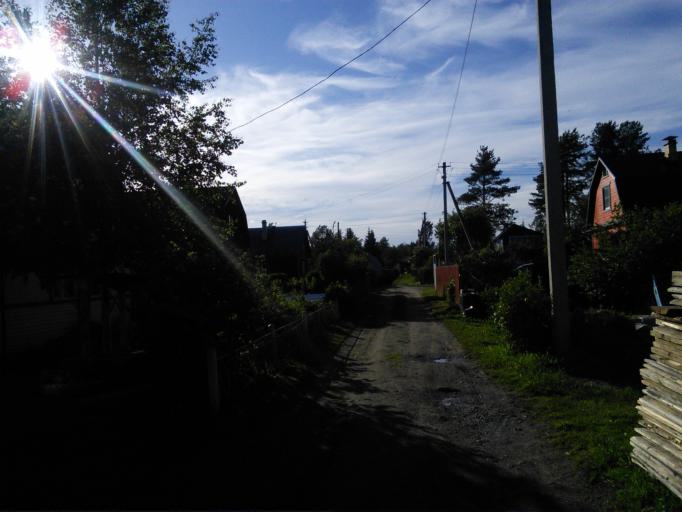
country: RU
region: Republic of Karelia
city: Shuya
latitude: 61.8498
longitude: 34.1436
